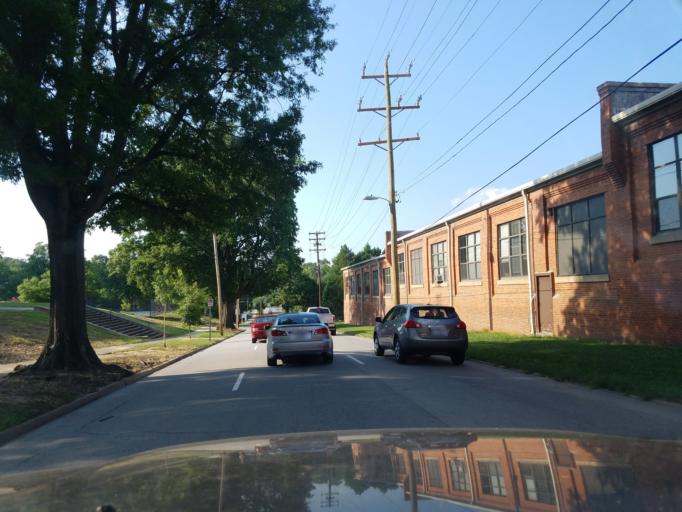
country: US
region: North Carolina
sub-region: Durham County
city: Durham
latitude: 36.0036
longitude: -78.9056
